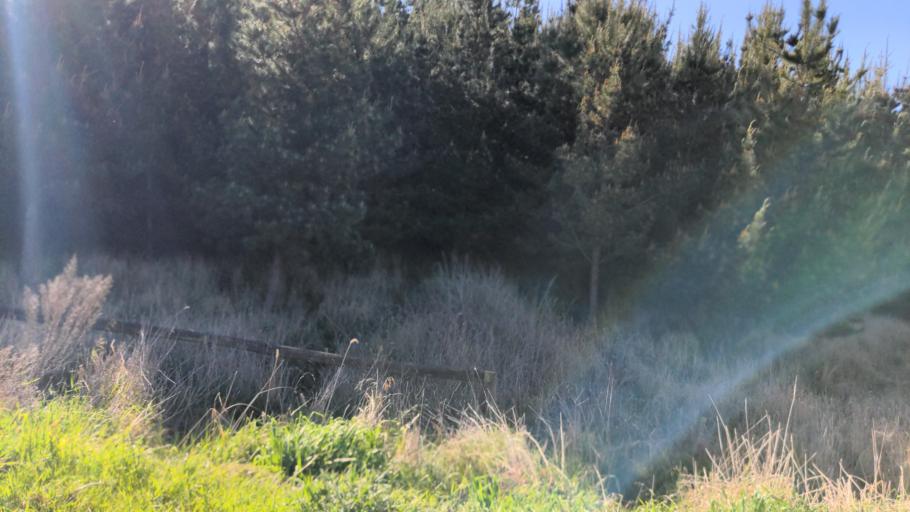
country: AU
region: New South Wales
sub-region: Blayney
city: Blayney
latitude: -33.4136
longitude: 149.3155
